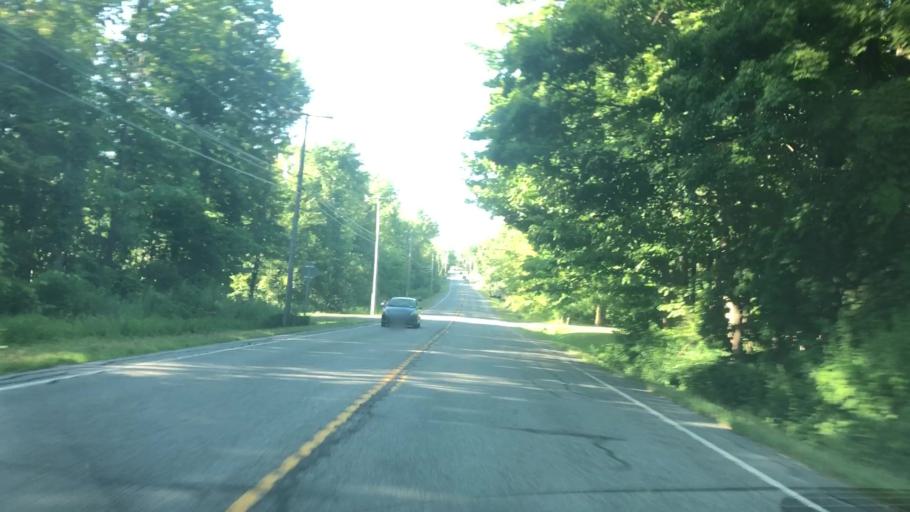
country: US
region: New York
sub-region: Wayne County
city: Ontario
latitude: 43.1538
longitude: -77.2925
